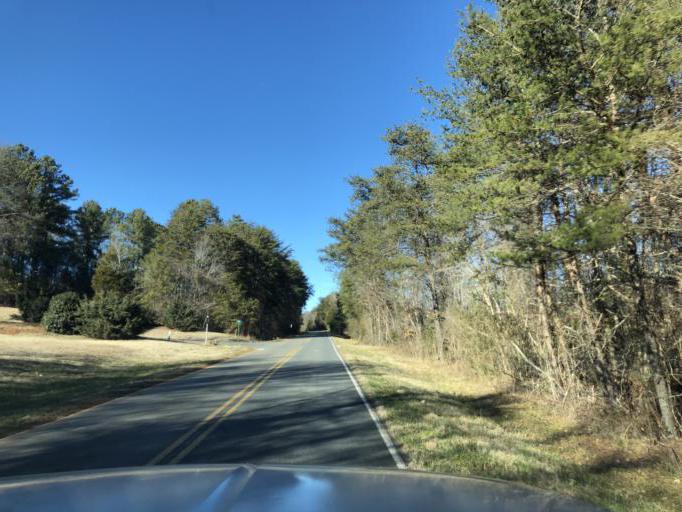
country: US
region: North Carolina
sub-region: Cleveland County
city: Shelby
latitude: 35.3320
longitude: -81.5393
